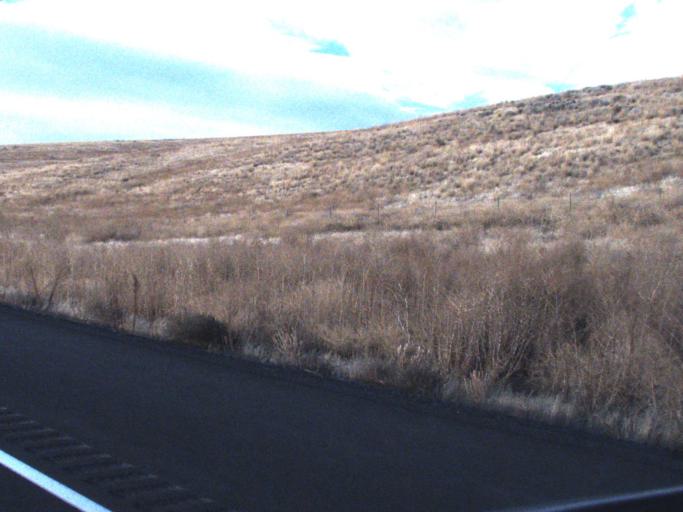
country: US
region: Washington
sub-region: Adams County
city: Ritzville
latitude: 46.8994
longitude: -118.6143
